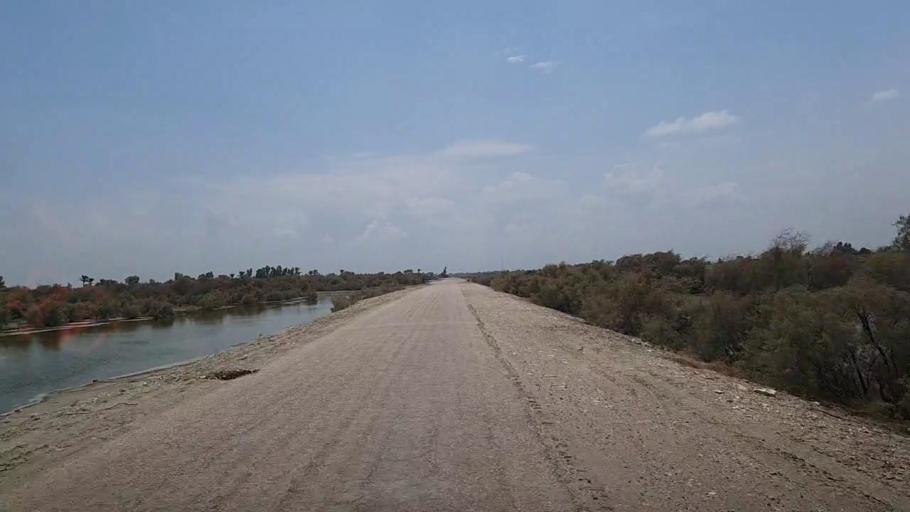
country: PK
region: Sindh
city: Kandhkot
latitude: 28.2836
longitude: 69.1683
